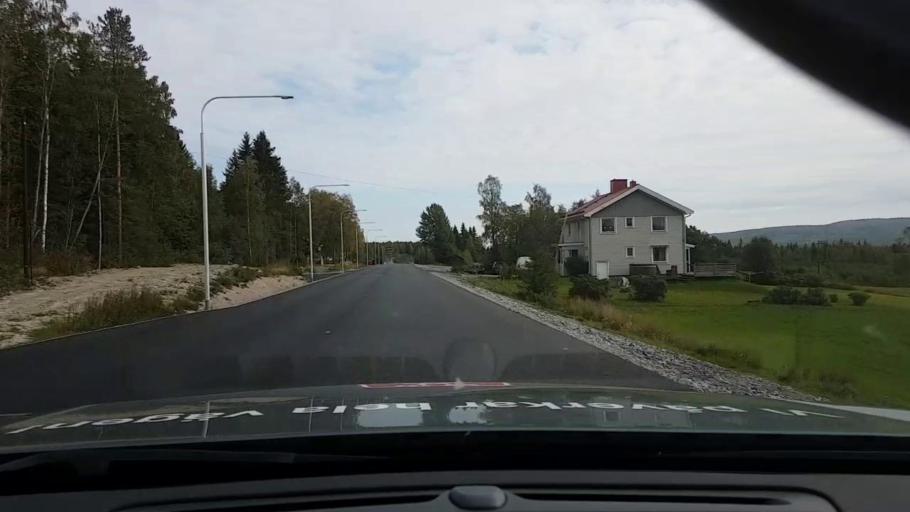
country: SE
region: Vaesternorrland
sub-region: OErnskoeldsviks Kommun
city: Bjasta
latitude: 63.2930
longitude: 18.4823
